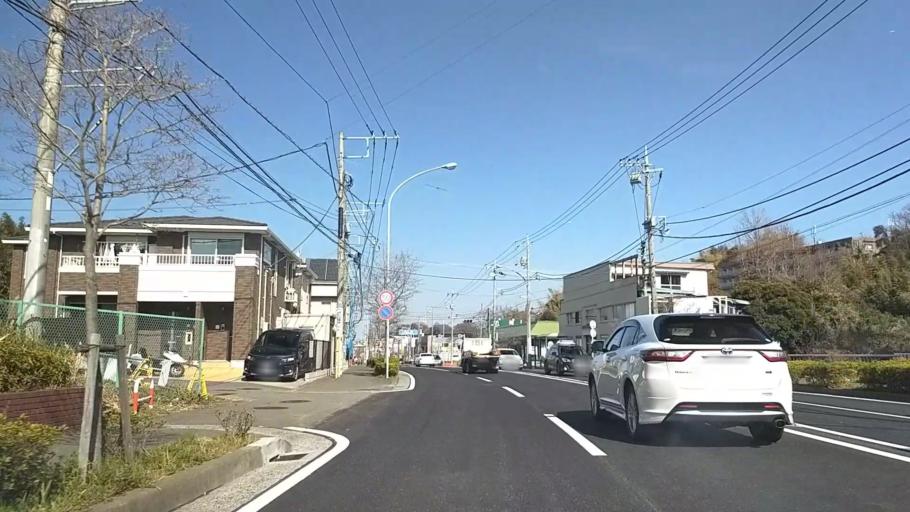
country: JP
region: Kanagawa
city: Zushi
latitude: 35.3680
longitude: 139.6134
